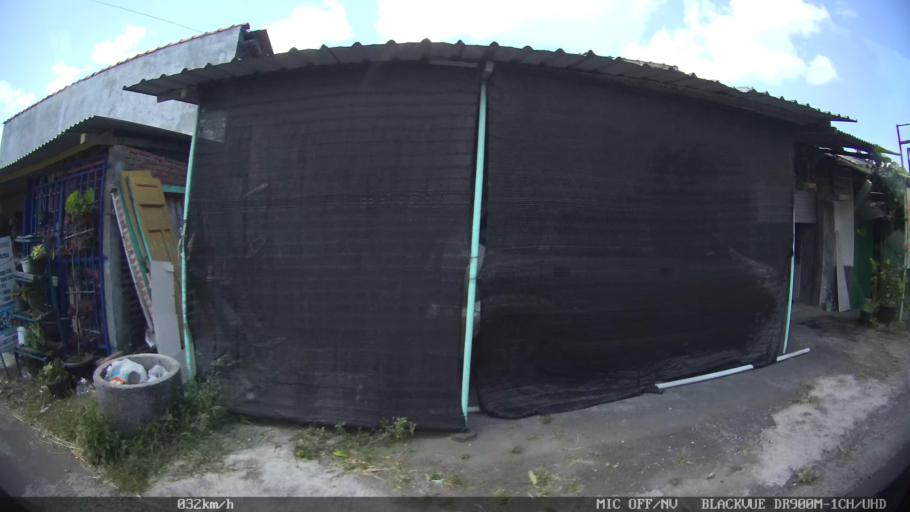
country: ID
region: Daerah Istimewa Yogyakarta
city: Sewon
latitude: -7.8754
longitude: 110.3755
